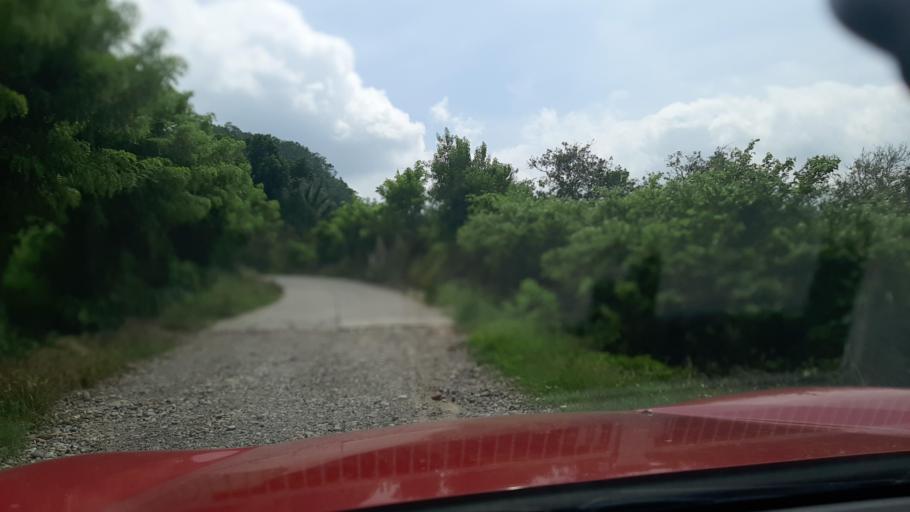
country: MX
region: Veracruz
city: Gutierrez Zamora
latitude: 20.4513
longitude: -97.1771
